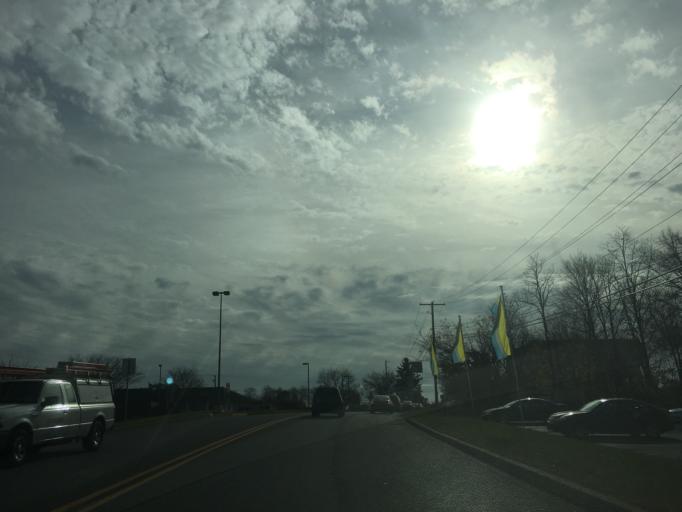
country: US
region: Pennsylvania
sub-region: Dauphin County
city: Colonial Park
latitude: 40.3008
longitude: -76.8209
